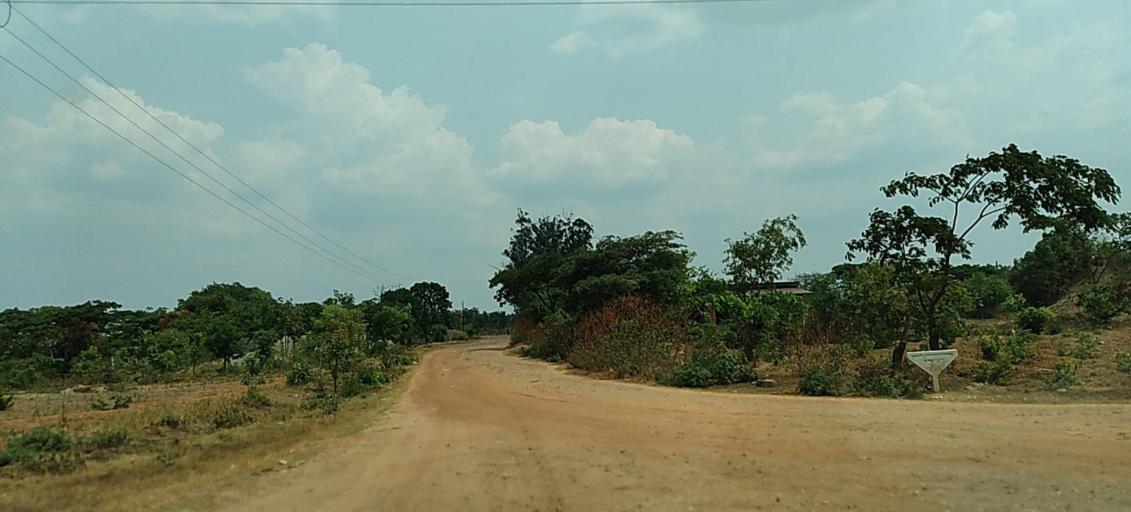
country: ZM
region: Copperbelt
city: Kalulushi
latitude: -12.8252
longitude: 28.0766
